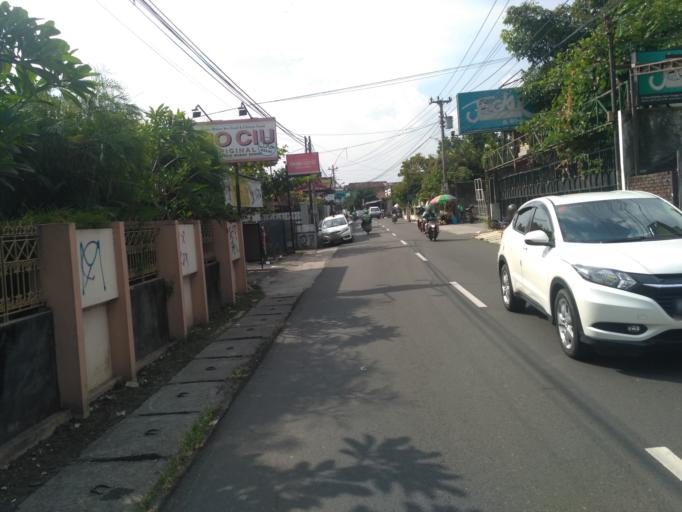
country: ID
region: Daerah Istimewa Yogyakarta
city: Depok
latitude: -7.7797
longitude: 110.4085
